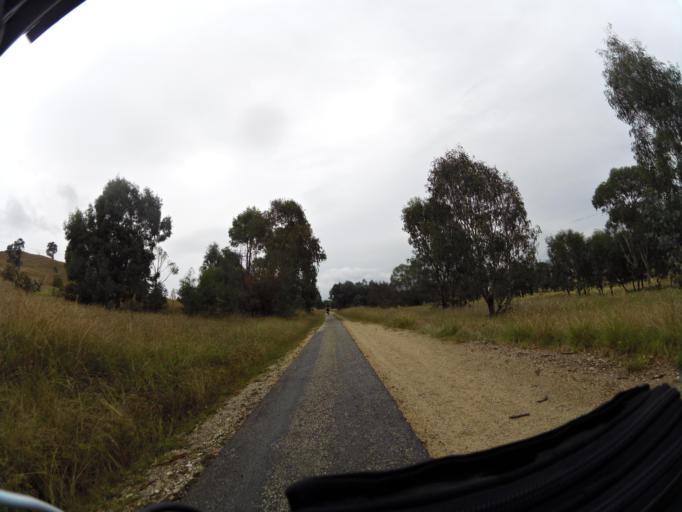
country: AU
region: New South Wales
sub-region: Albury Municipality
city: East Albury
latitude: -36.2241
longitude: 147.1079
